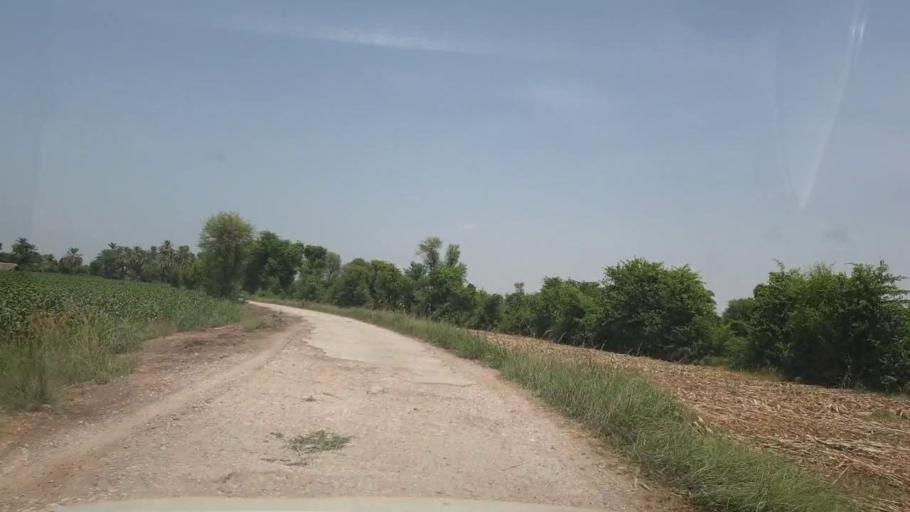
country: PK
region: Sindh
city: Bozdar
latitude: 27.1746
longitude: 68.6290
